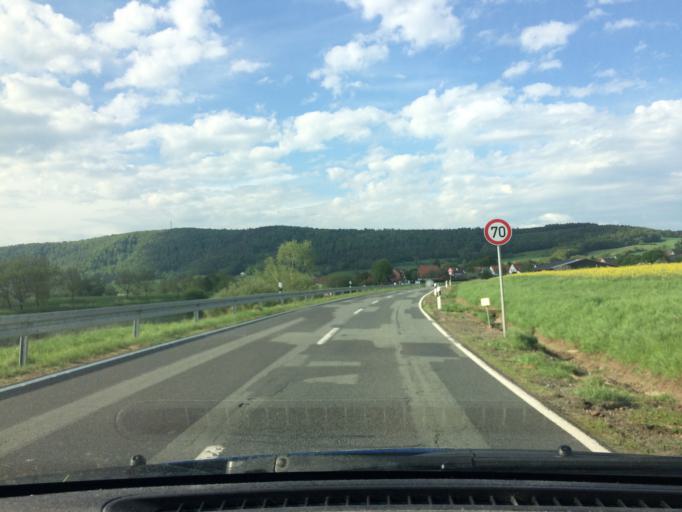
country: DE
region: Lower Saxony
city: Bodenfelde
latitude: 51.5834
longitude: 9.5942
